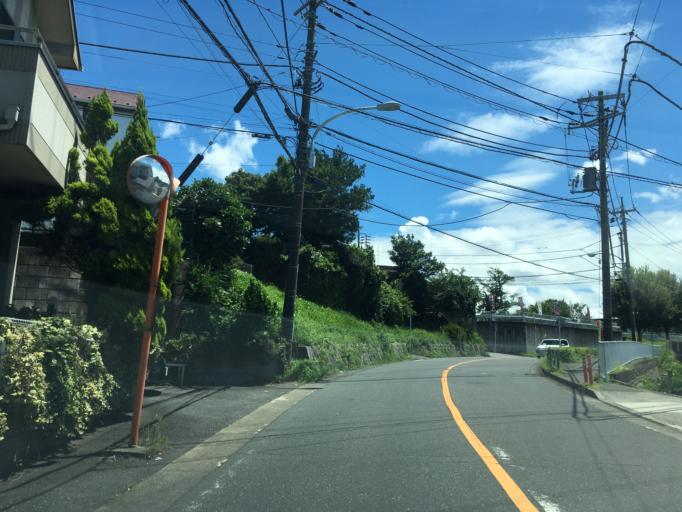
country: JP
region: Tokyo
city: Kokubunji
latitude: 35.6386
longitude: 139.4641
